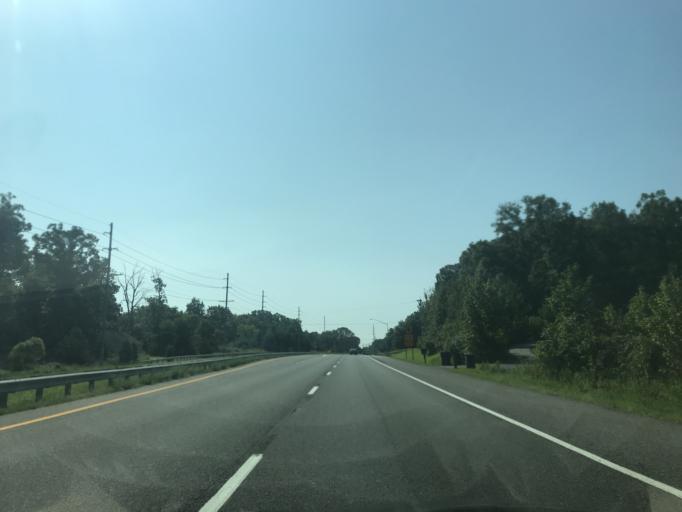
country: US
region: Maryland
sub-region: Charles County
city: Hughesville
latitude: 38.5190
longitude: -76.7764
